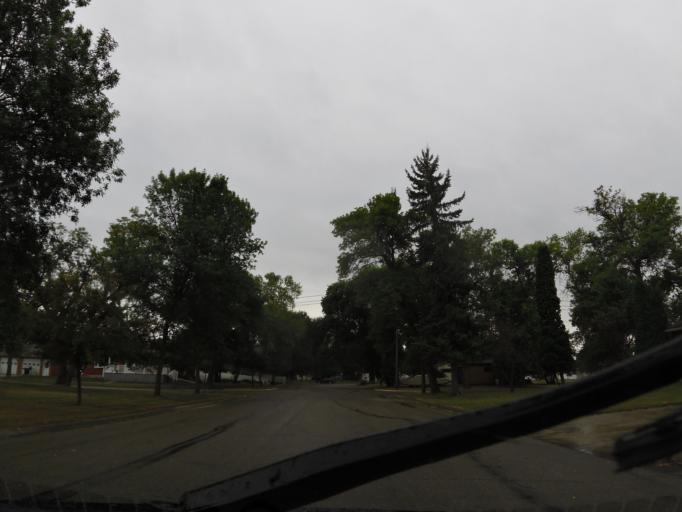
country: US
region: Minnesota
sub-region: Marshall County
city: Warren
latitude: 48.4502
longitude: -96.8709
